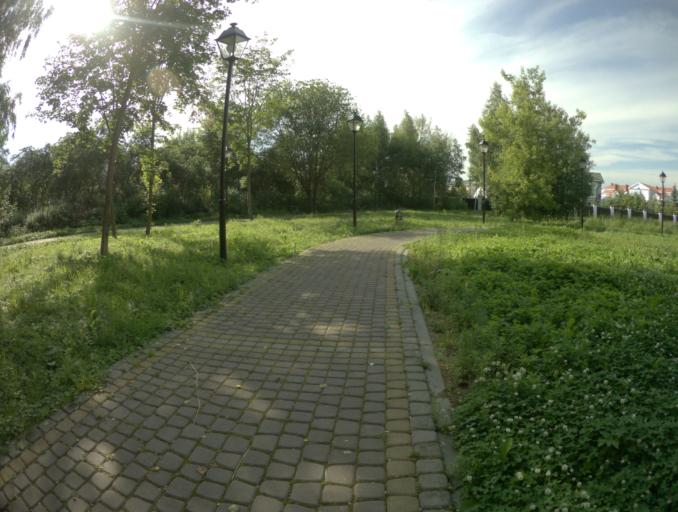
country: RU
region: Vladimir
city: Suzdal'
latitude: 56.4299
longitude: 40.4465
